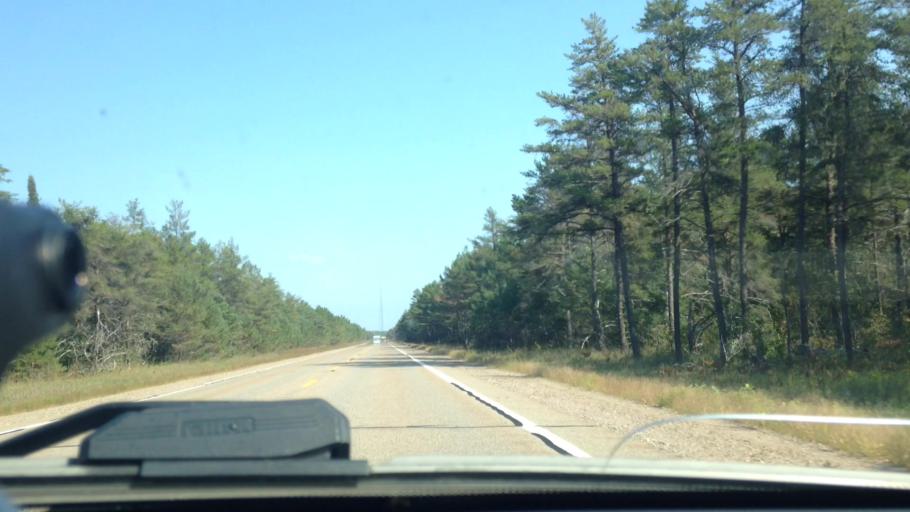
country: US
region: Michigan
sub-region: Chippewa County
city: Sault Ste. Marie
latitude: 46.3587
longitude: -84.8184
